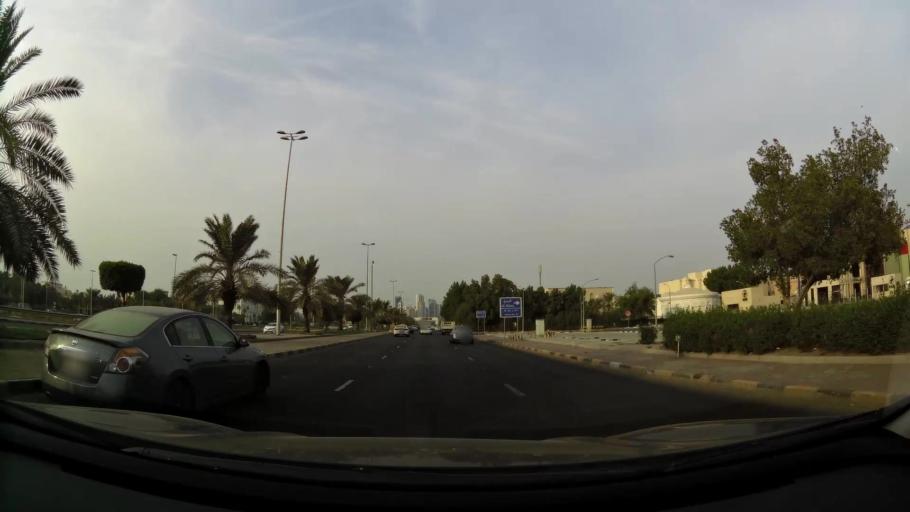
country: KW
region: Muhafazat Hawalli
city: Ar Rumaythiyah
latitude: 29.3139
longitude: 48.0870
